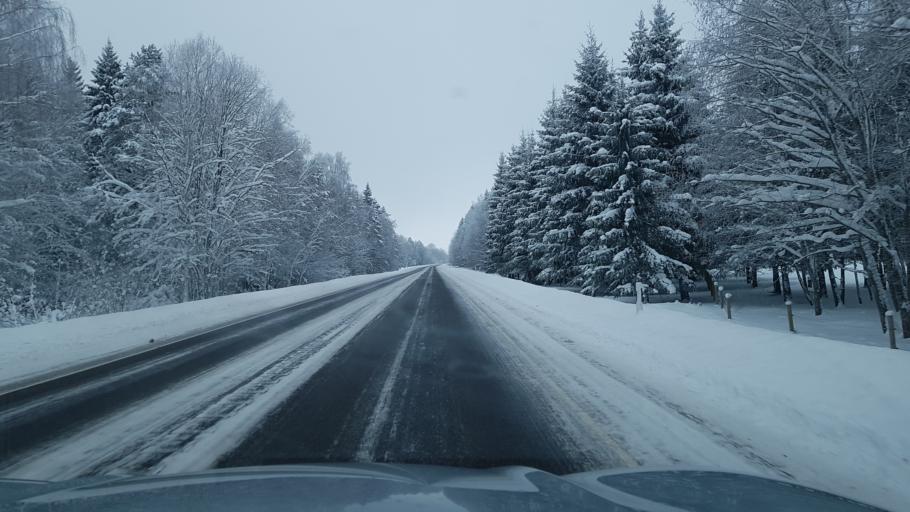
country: EE
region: Ida-Virumaa
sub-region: Johvi vald
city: Johvi
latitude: 59.3010
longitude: 27.3956
